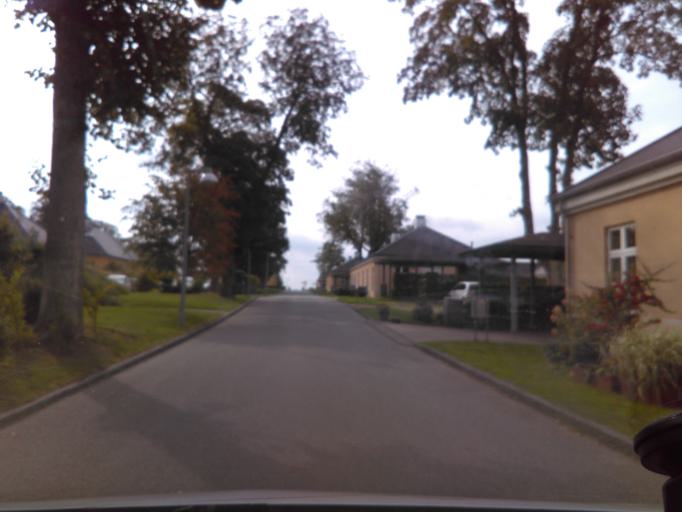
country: DK
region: Capital Region
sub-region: Ballerup Kommune
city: Malov
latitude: 55.7762
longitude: 12.3196
